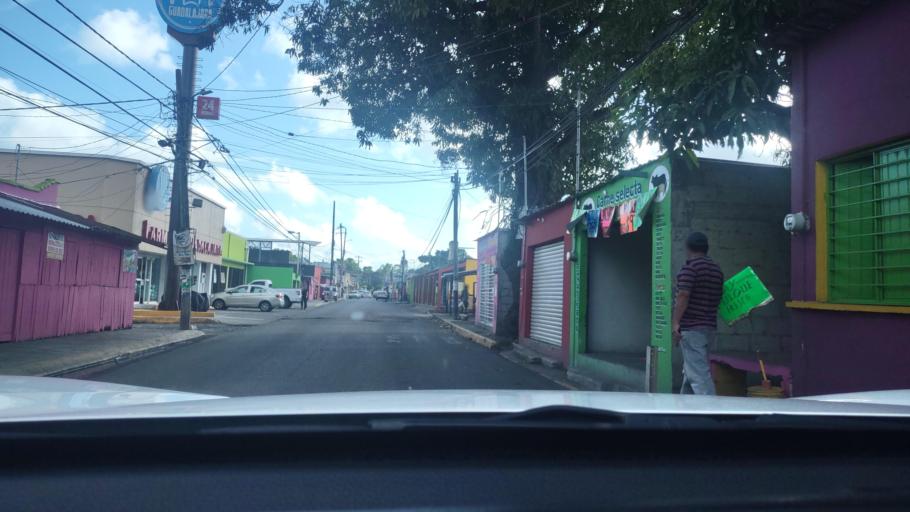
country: MX
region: Veracruz
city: El Tejar
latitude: 19.0719
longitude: -96.1616
